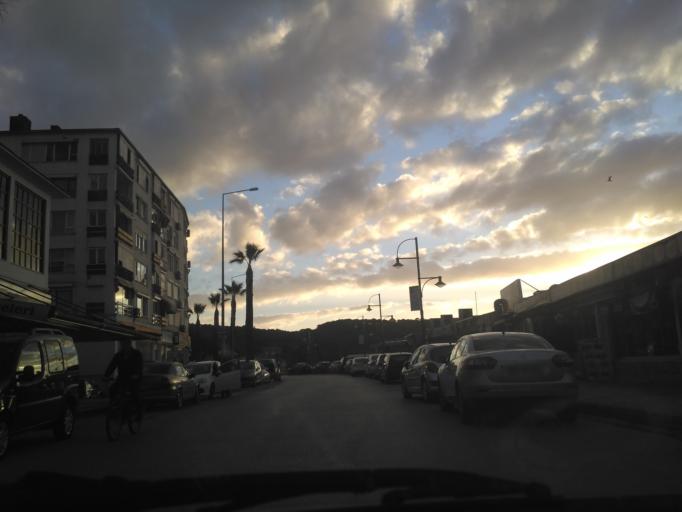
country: TR
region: Balikesir
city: Ayvalik
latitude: 39.3158
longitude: 26.6906
